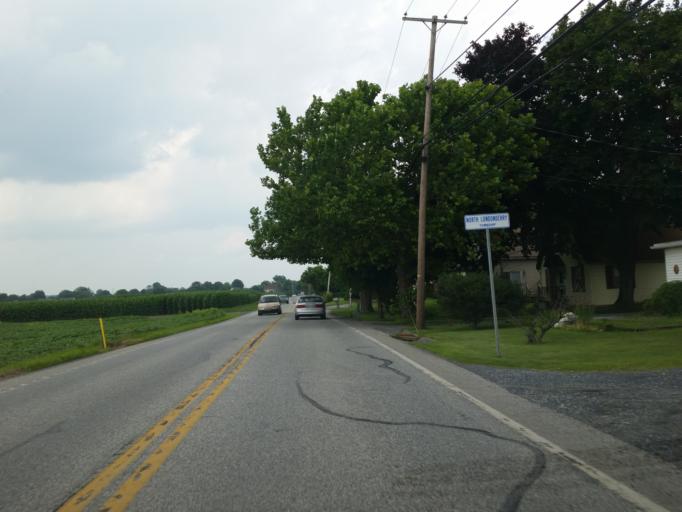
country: US
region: Pennsylvania
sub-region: Lebanon County
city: Campbelltown
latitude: 40.2918
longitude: -76.5754
